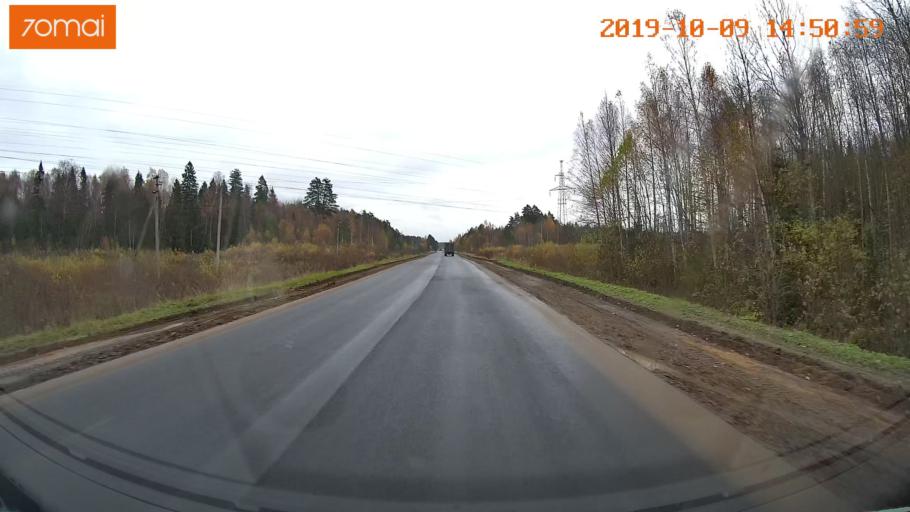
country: RU
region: Kostroma
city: Chistyye Bory
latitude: 58.3799
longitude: 41.6088
